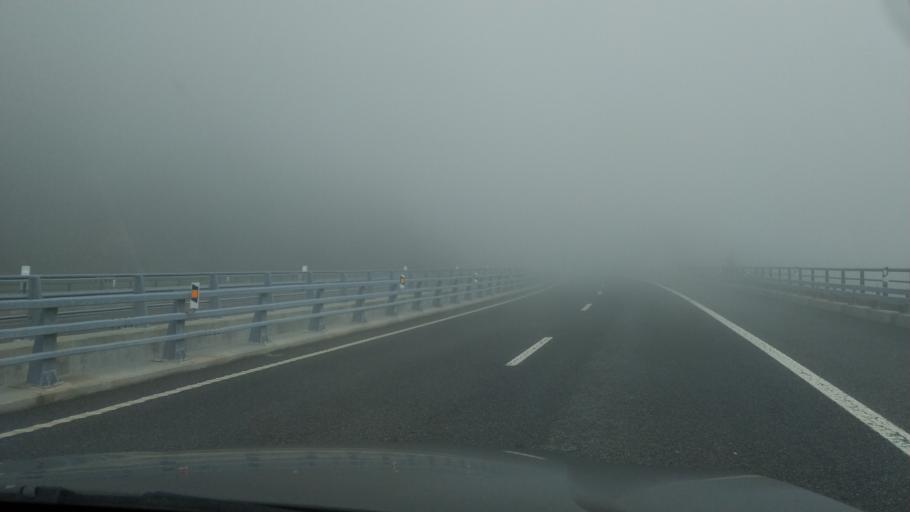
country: PT
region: Vila Real
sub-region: Vila Pouca de Aguiar
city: Vila Pouca de Aguiar
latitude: 41.5323
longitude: -7.6337
